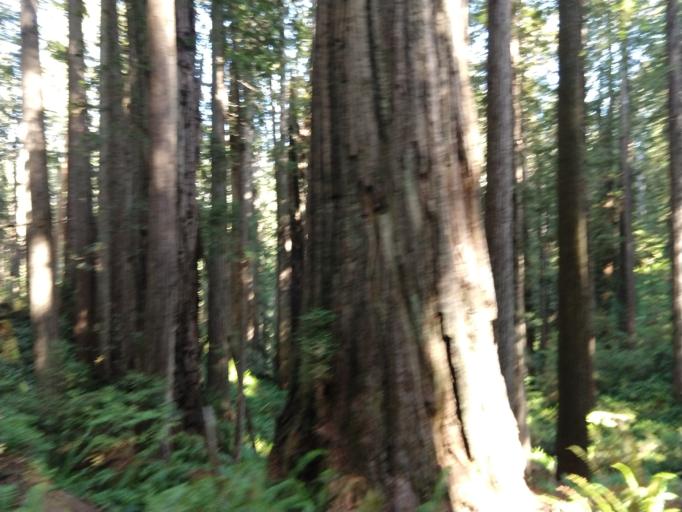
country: US
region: California
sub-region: Humboldt County
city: Westhaven-Moonstone
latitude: 41.3892
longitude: -124.0526
